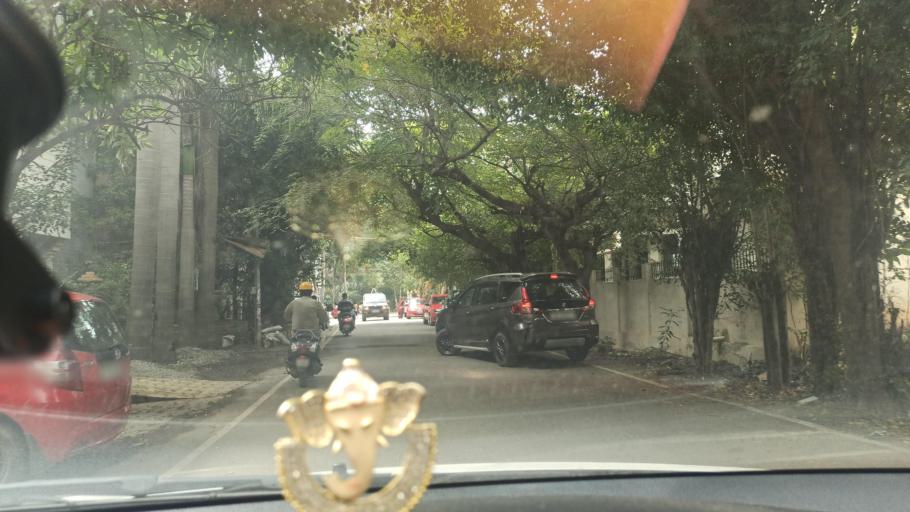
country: IN
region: Karnataka
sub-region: Bangalore Urban
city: Bangalore
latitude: 12.9172
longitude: 77.6472
